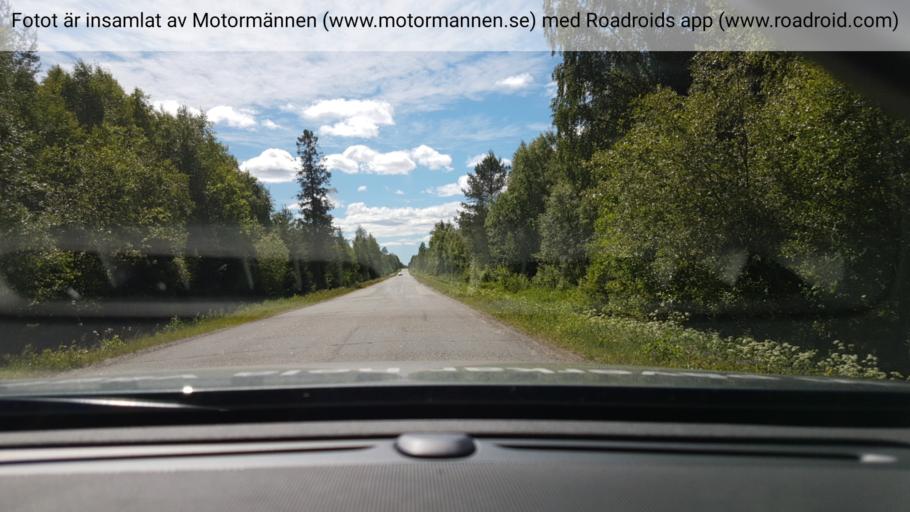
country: SE
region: Vaesterbotten
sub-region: Skelleftea Kommun
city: Burea
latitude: 64.4420
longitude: 21.3546
